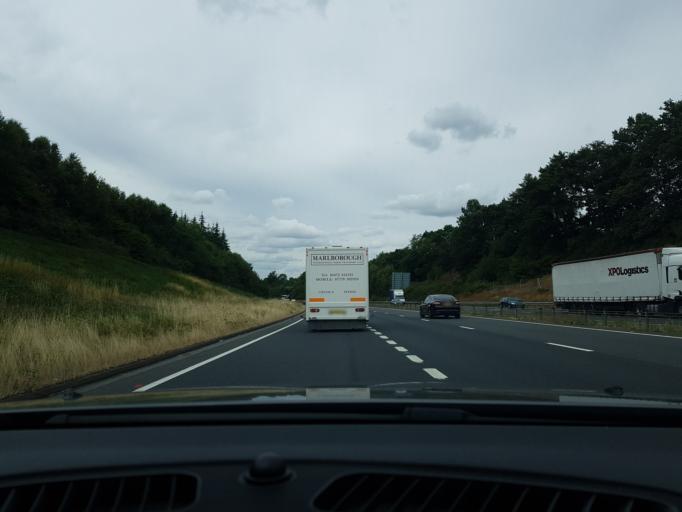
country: GB
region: England
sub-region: Hampshire
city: Highclere
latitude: 51.3521
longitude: -1.3400
